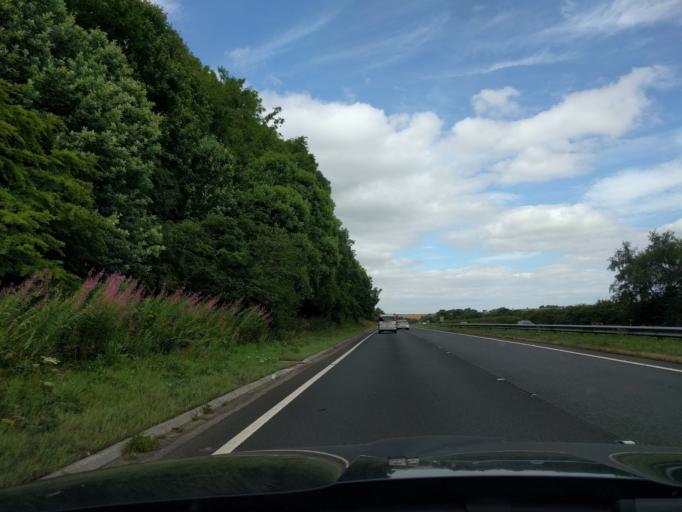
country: GB
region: England
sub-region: Northumberland
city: Felton
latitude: 55.3411
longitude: -1.7268
